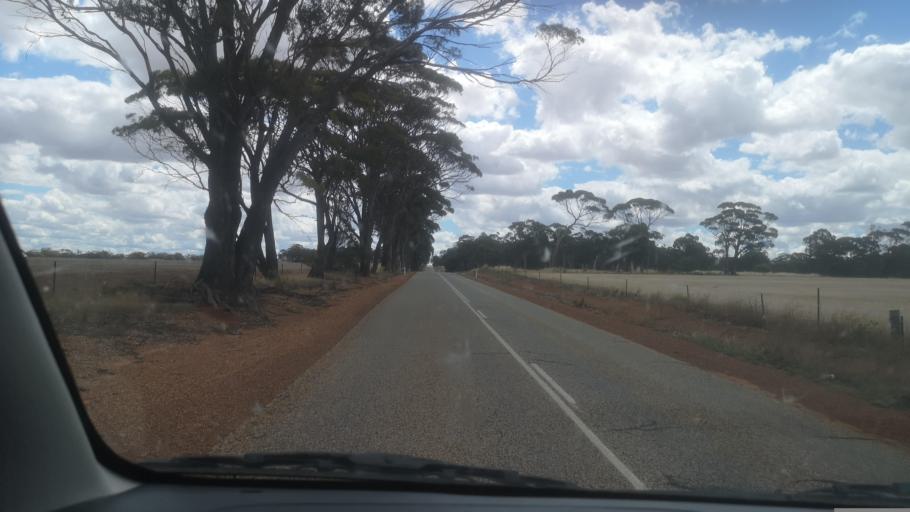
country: AU
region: Western Australia
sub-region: Beverley
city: Beverley
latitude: -31.9900
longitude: 117.1164
